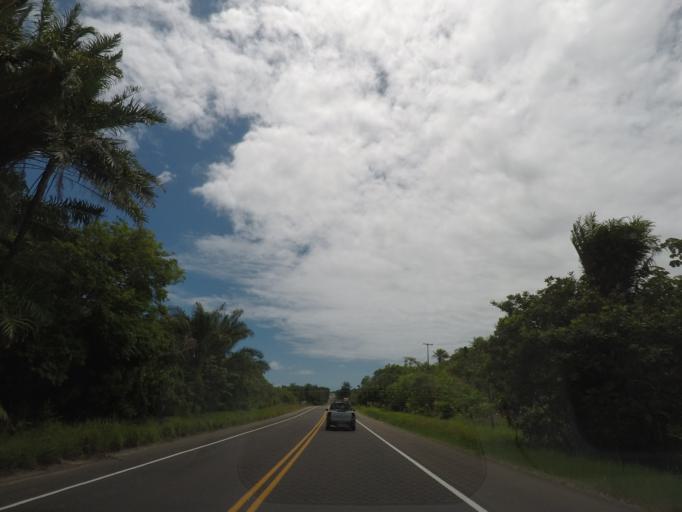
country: BR
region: Bahia
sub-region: Itaparica
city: Itaparica
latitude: -12.9665
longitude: -38.6358
